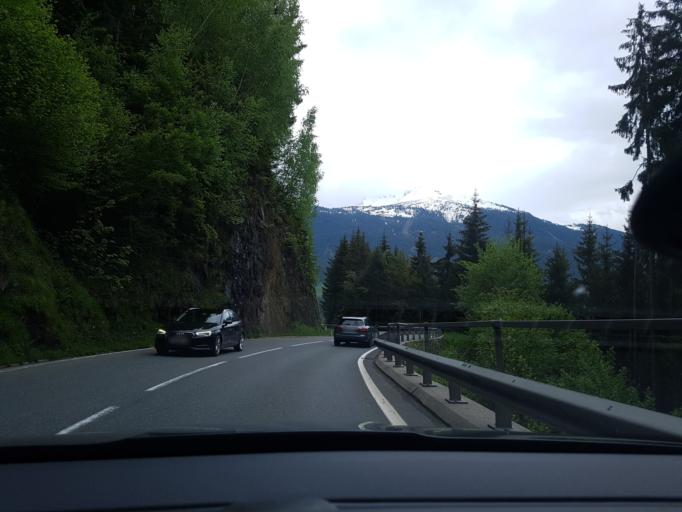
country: AT
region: Salzburg
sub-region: Politischer Bezirk Zell am See
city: Mittersill
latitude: 47.2922
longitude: 12.4464
